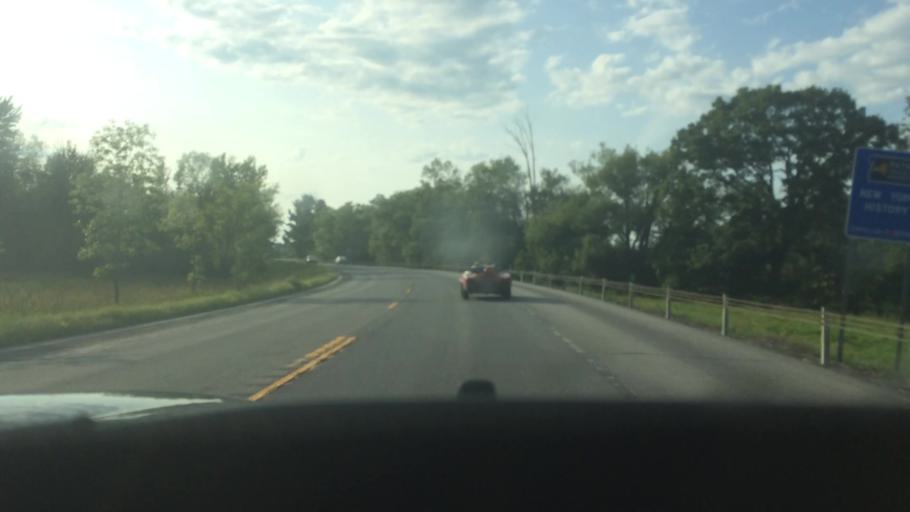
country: US
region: New York
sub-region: St. Lawrence County
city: Canton
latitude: 44.6184
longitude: -75.2229
